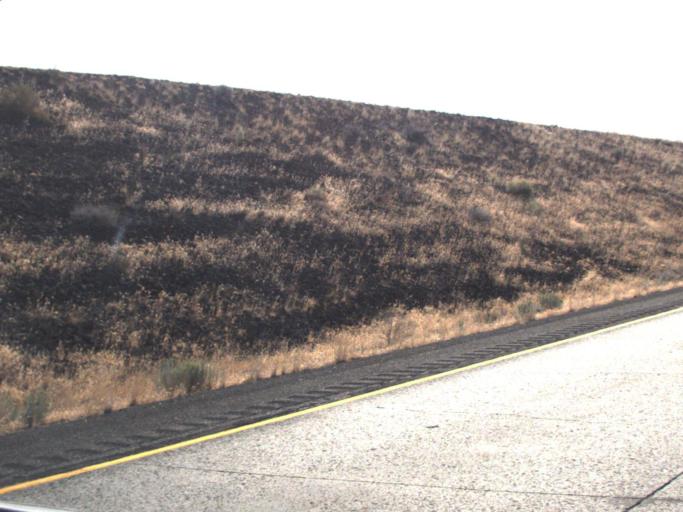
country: US
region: Washington
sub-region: Kittitas County
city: Kittitas
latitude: 46.8856
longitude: -120.4276
